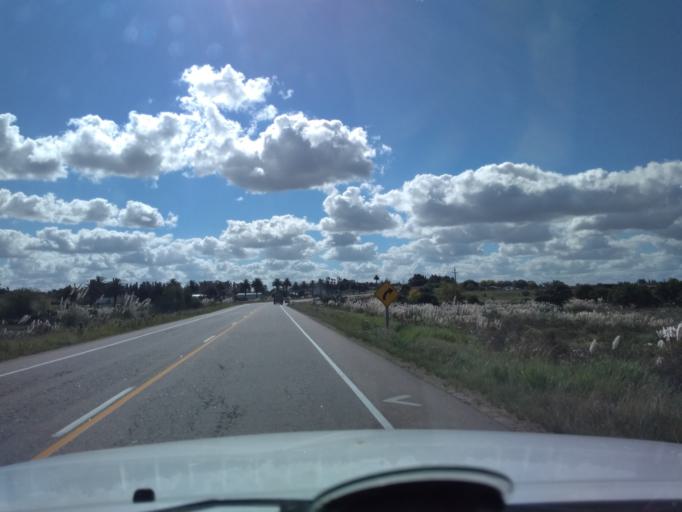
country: UY
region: Canelones
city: Sauce
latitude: -34.6710
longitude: -56.0541
